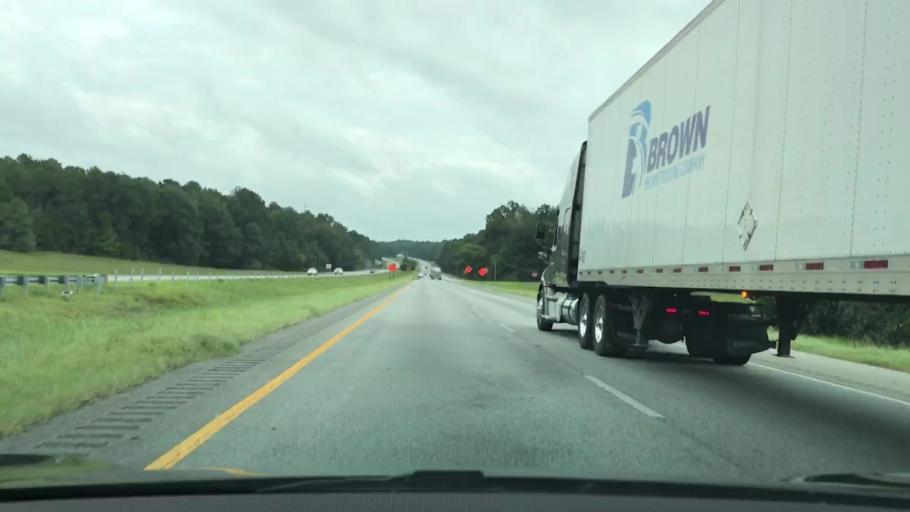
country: US
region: Alabama
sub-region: Macon County
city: Tuskegee
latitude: 32.4871
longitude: -85.6362
